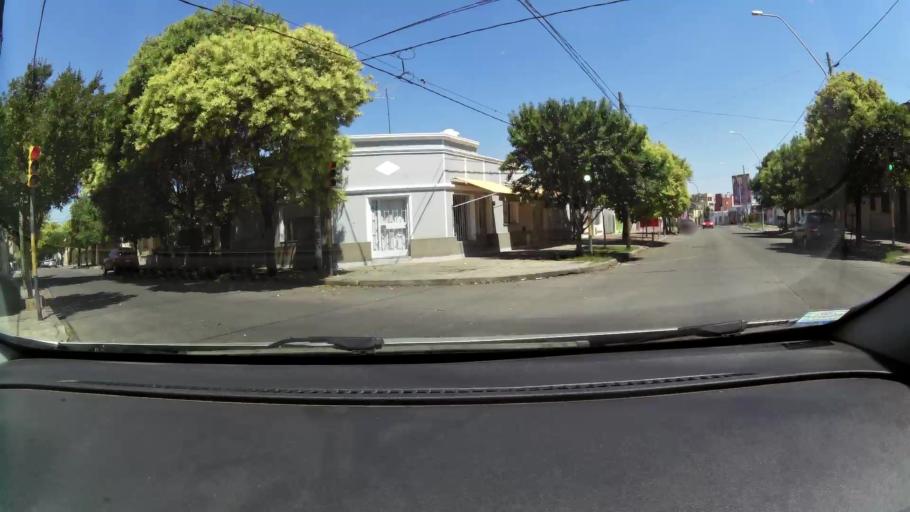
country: AR
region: Cordoba
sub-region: Departamento de Capital
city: Cordoba
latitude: -31.3817
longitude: -64.1990
